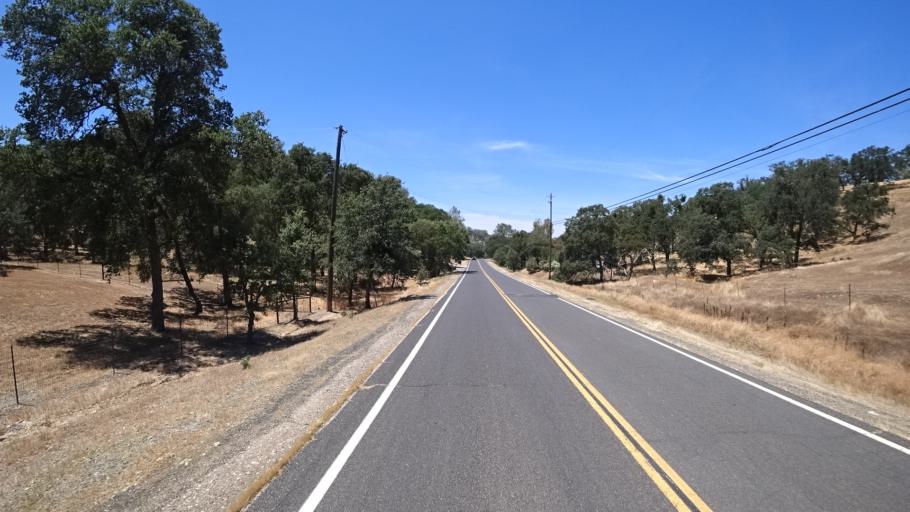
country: US
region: California
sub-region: Calaveras County
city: Rancho Calaveras
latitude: 38.1391
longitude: -120.8567
